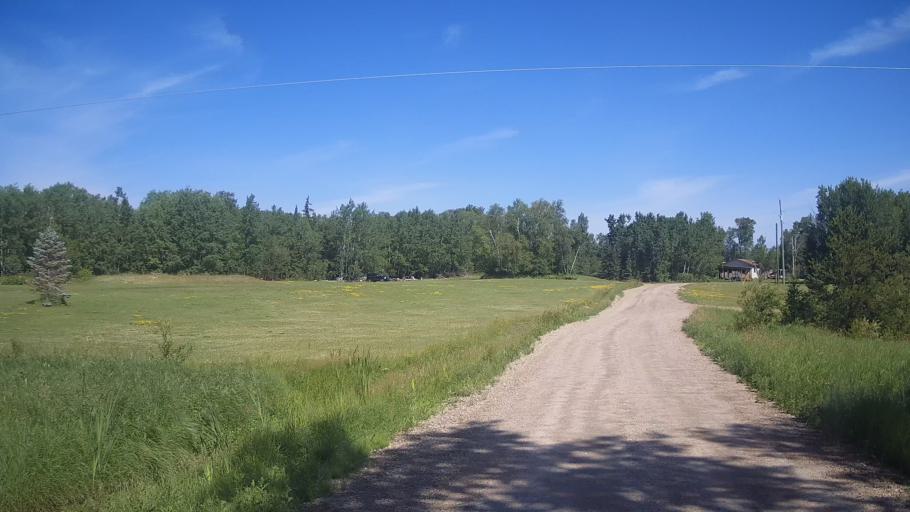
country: CA
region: Ontario
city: Dryden
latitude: 49.8214
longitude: -93.3384
